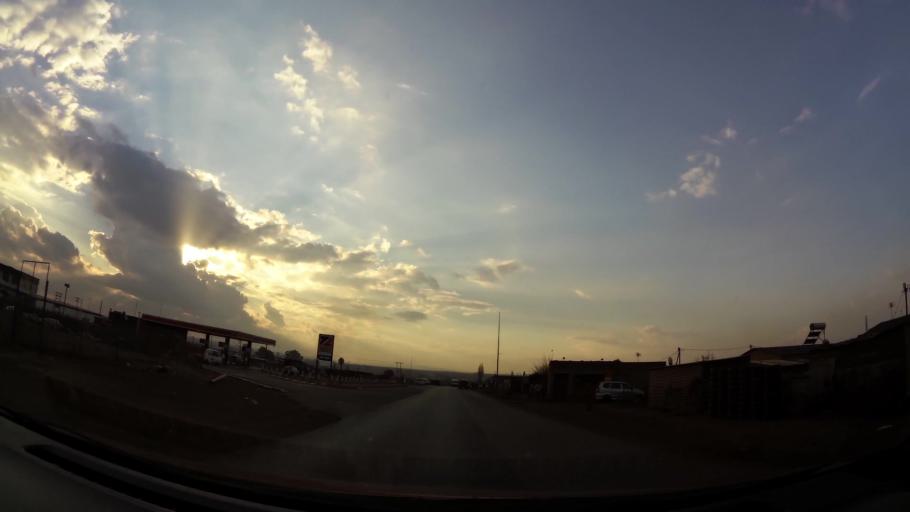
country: ZA
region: Gauteng
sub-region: City of Johannesburg Metropolitan Municipality
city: Orange Farm
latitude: -26.5580
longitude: 27.8311
